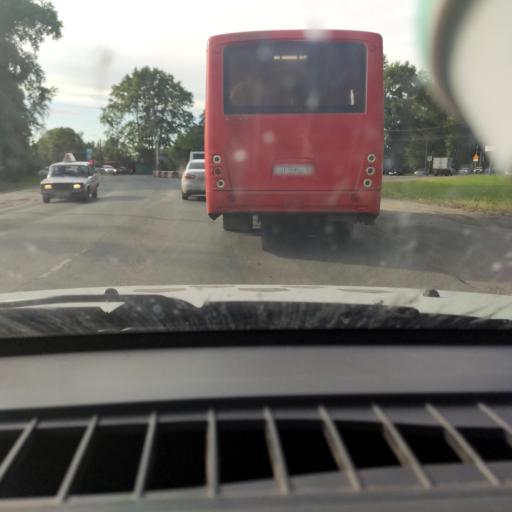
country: RU
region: Kirov
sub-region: Kirovo-Chepetskiy Rayon
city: Kirov
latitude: 58.6146
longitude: 49.7417
